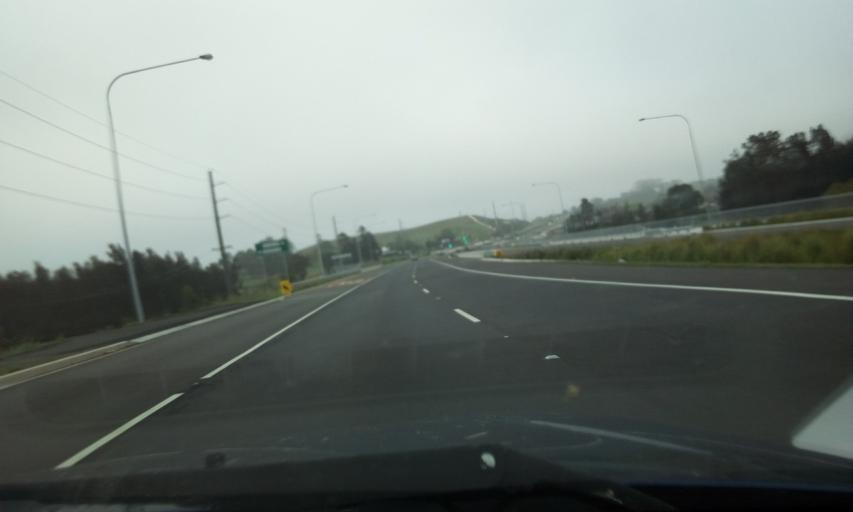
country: AU
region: New South Wales
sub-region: Camden
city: Narellan
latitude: -34.0295
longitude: 150.7275
